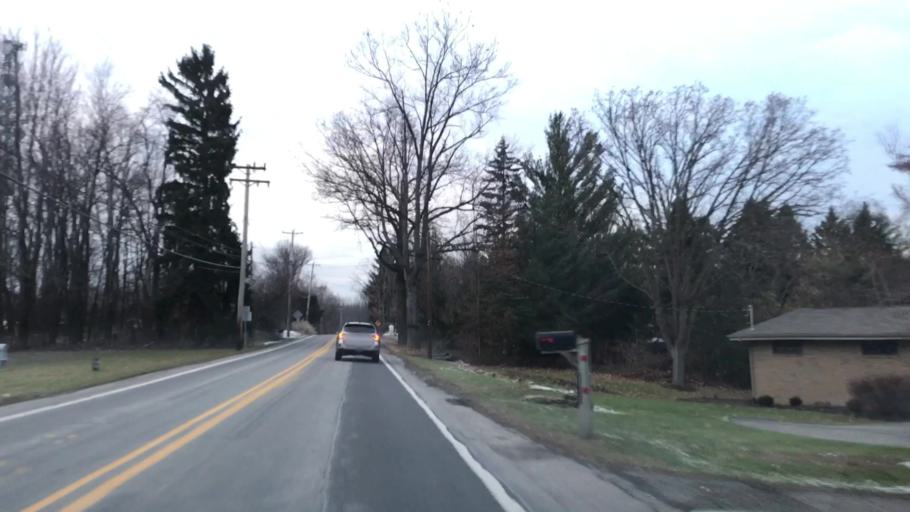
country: US
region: Pennsylvania
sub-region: Allegheny County
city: Gibsonia
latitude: 40.6342
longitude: -80.0048
